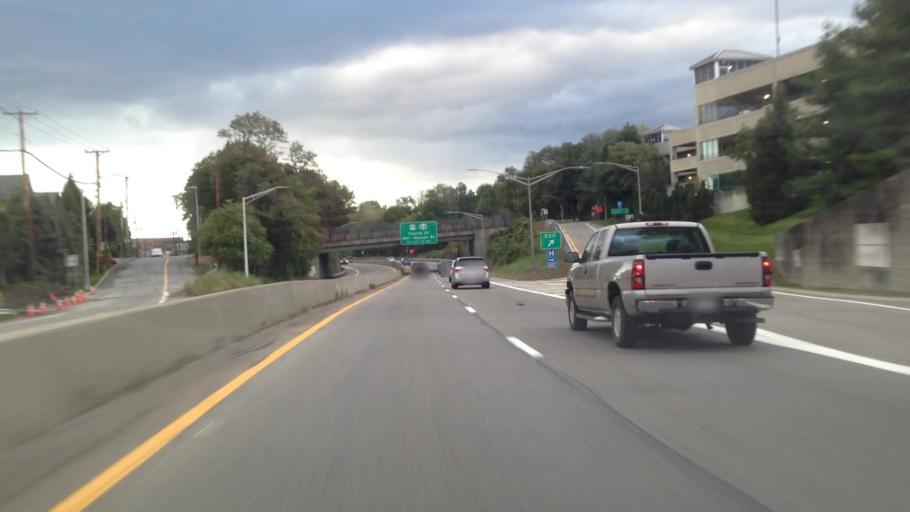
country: US
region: New York
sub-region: Dutchess County
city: Poughkeepsie
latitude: 41.6944
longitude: -73.9373
